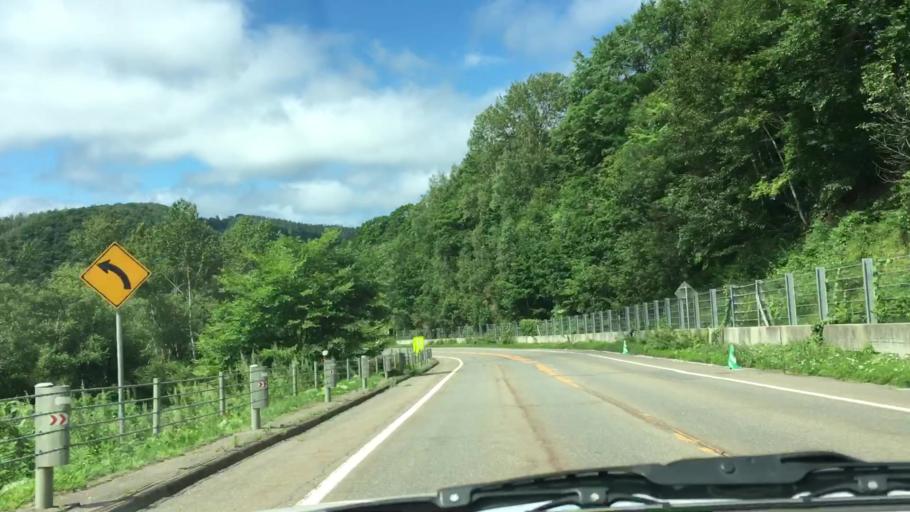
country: JP
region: Hokkaido
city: Kitami
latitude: 43.3530
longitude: 143.7932
